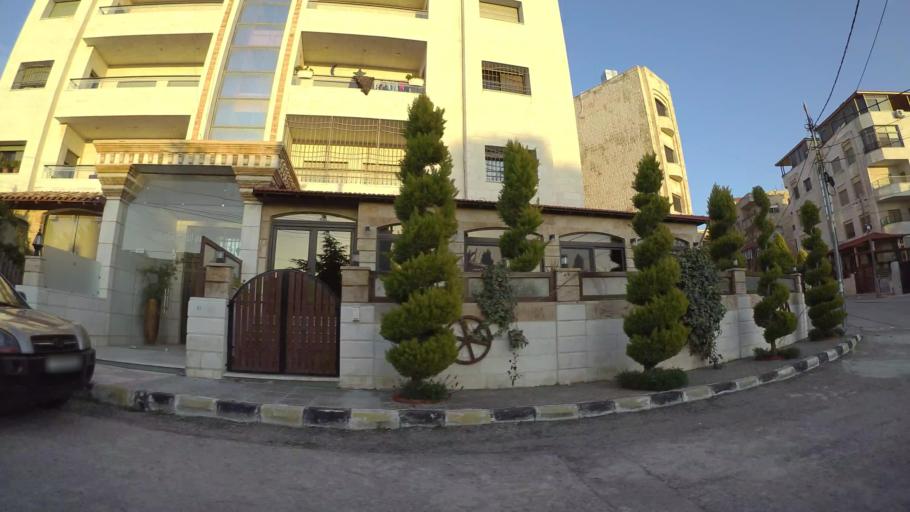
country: JO
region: Amman
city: Al Jubayhah
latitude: 31.9922
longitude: 35.8755
